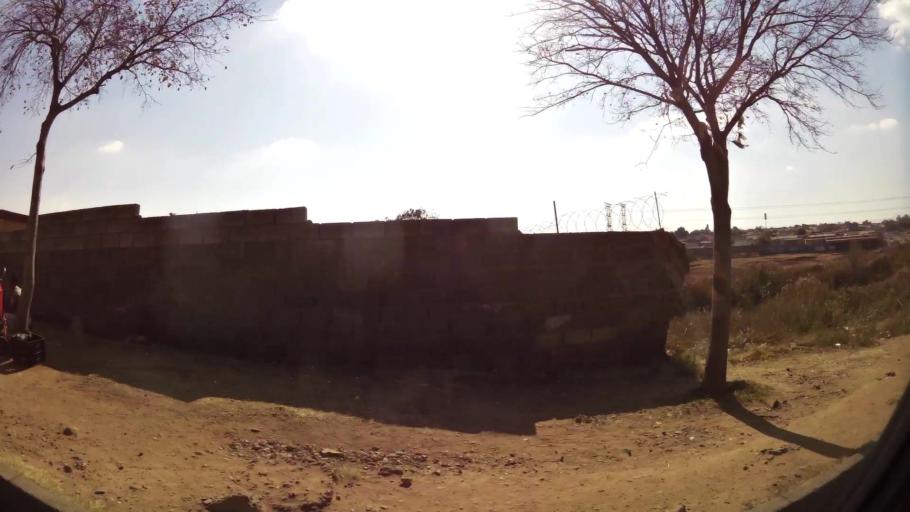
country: ZA
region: Gauteng
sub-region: City of Johannesburg Metropolitan Municipality
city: Soweto
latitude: -26.2554
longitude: 27.9435
